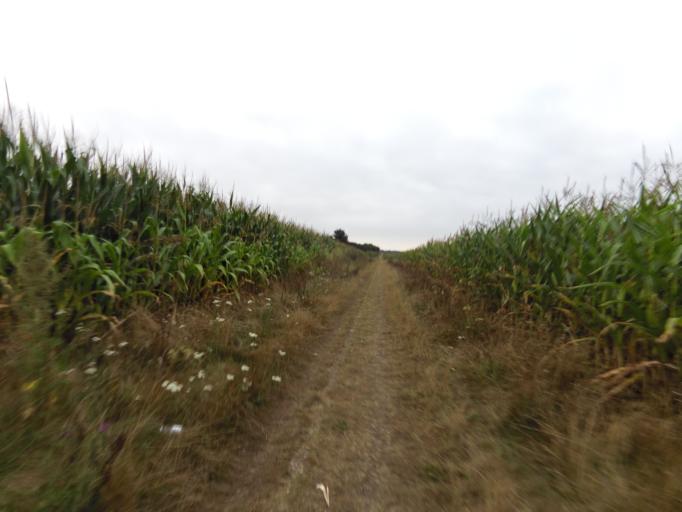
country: GB
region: England
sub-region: Hertfordshire
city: Radlett
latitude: 51.7196
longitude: -0.3168
